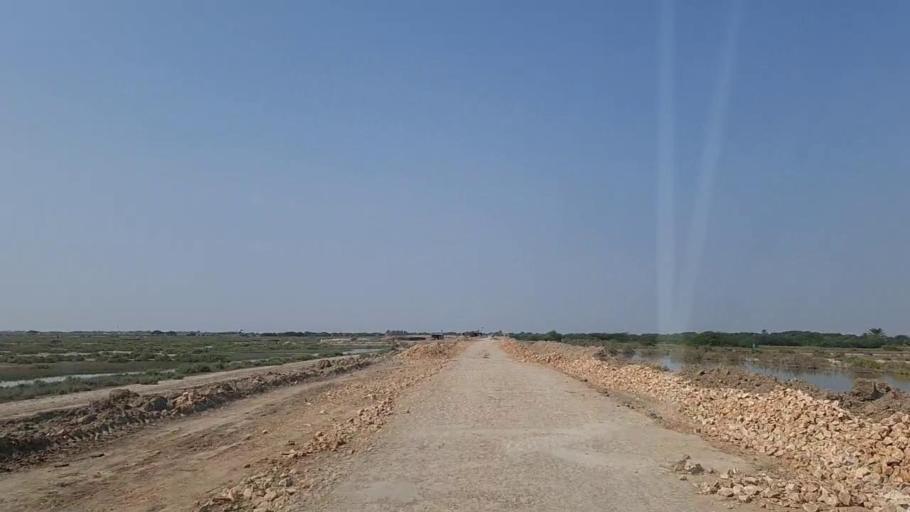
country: PK
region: Sindh
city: Chuhar Jamali
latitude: 24.1939
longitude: 67.8395
